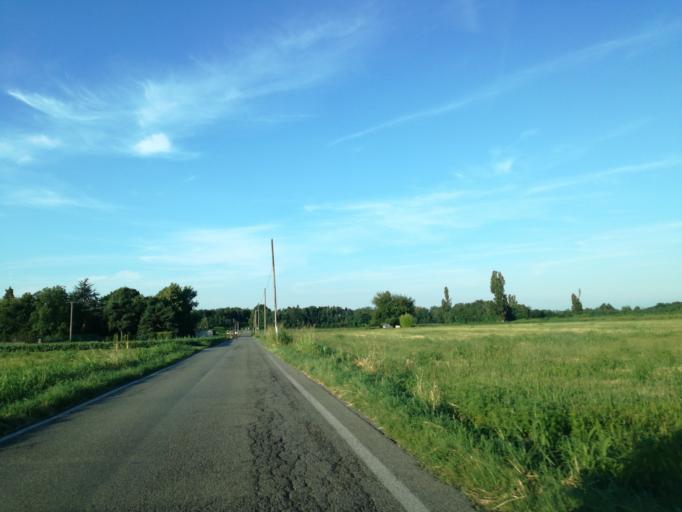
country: IT
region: Lombardy
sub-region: Provincia di Lecco
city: Verderio Inferiore
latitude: 45.6590
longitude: 9.4322
